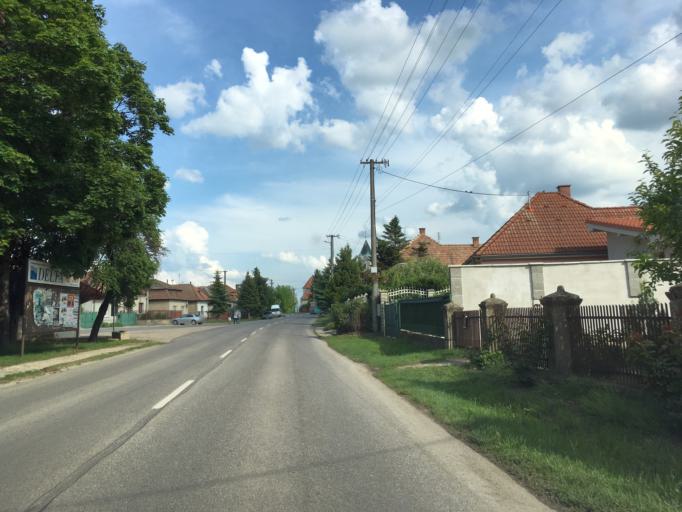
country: HU
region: Komarom-Esztergom
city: Almasfuzito
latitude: 47.7880
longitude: 18.2705
